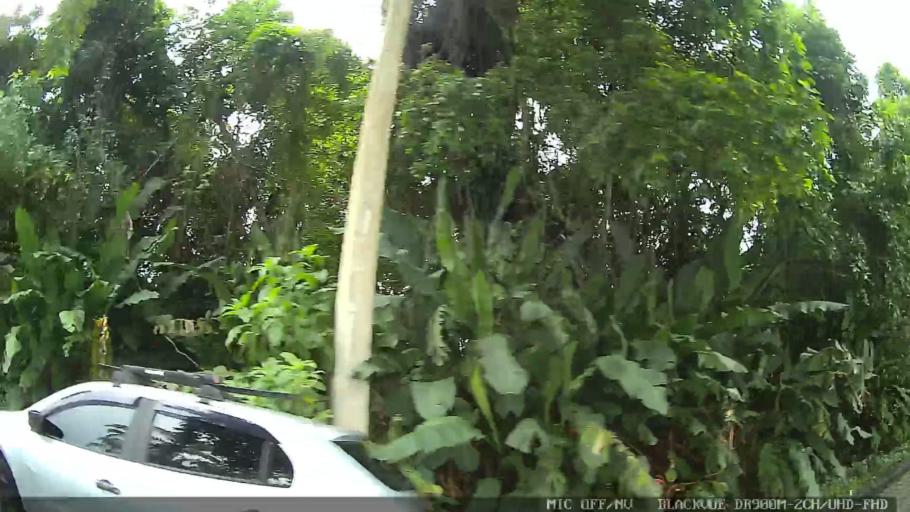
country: BR
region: Sao Paulo
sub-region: Caraguatatuba
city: Caraguatatuba
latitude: -23.6214
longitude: -45.3858
